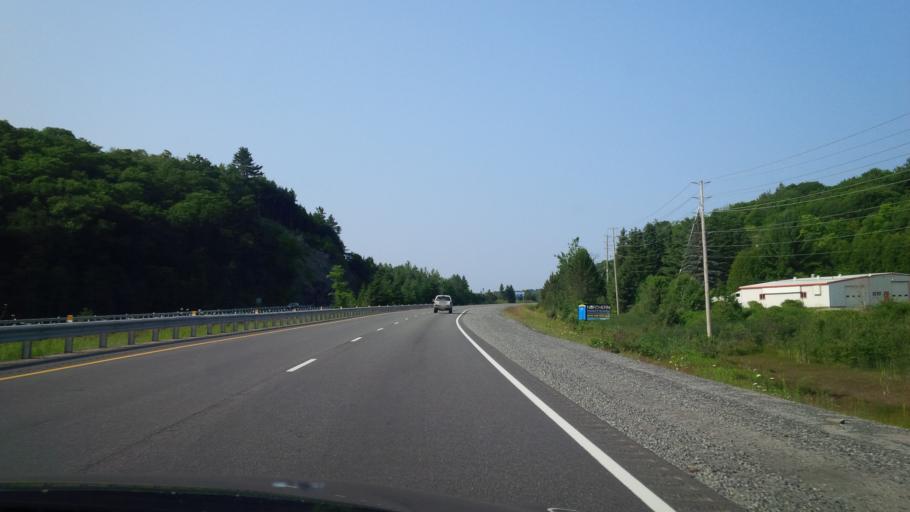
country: CA
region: Ontario
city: Huntsville
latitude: 45.3075
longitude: -79.2469
